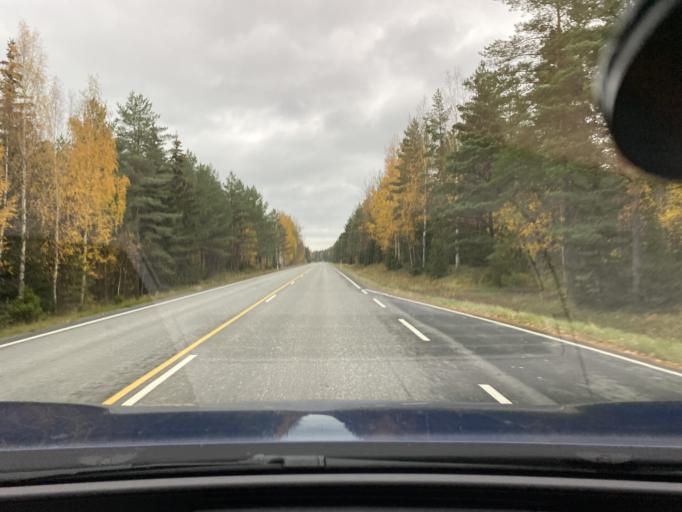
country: FI
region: Varsinais-Suomi
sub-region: Loimaa
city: Ylaene
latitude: 60.9103
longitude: 22.4122
